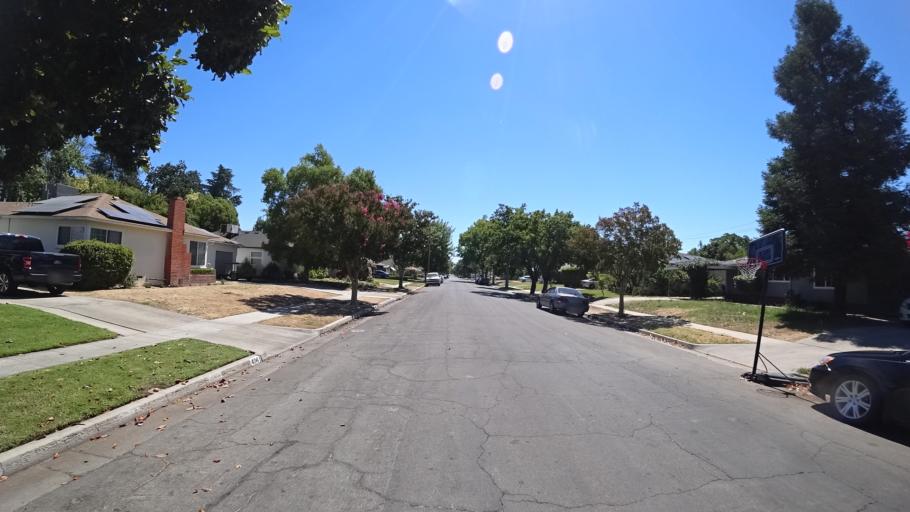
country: US
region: California
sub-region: Fresno County
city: Fresno
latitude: 36.7830
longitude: -119.8165
